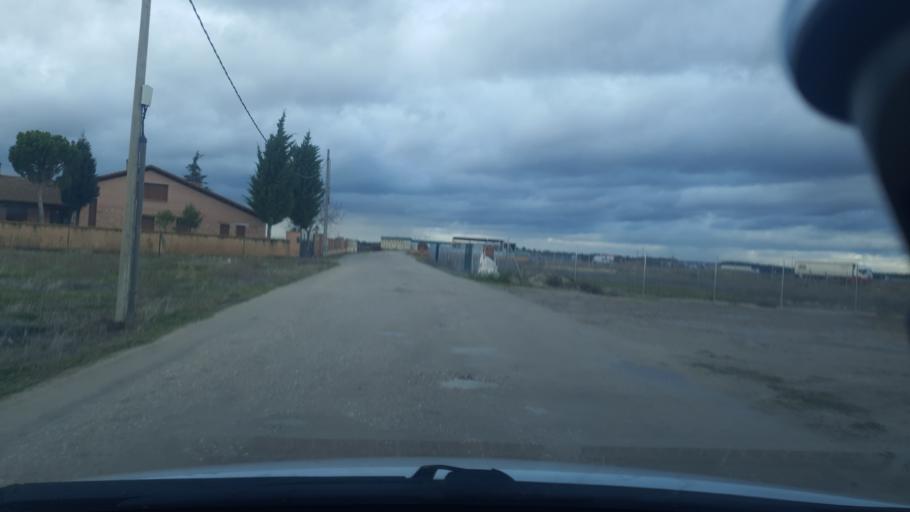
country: ES
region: Castille and Leon
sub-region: Provincia de Segovia
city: Sanchonuno
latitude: 41.2909
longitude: -4.3290
